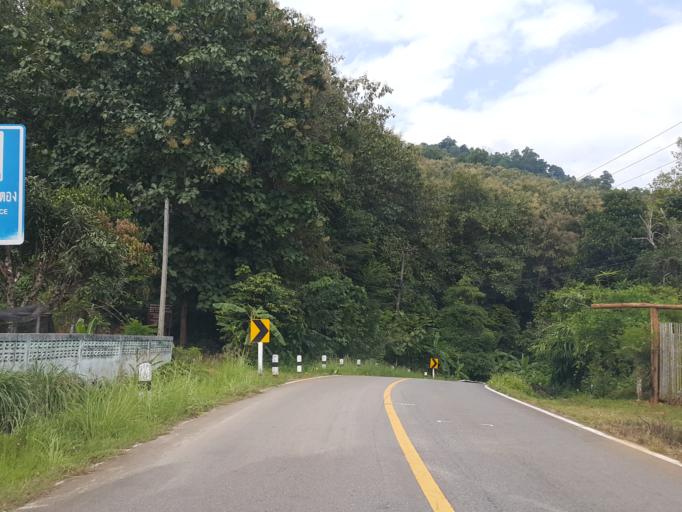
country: TH
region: Mae Hong Son
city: Mae Hong Son
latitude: 19.4703
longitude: 97.9656
